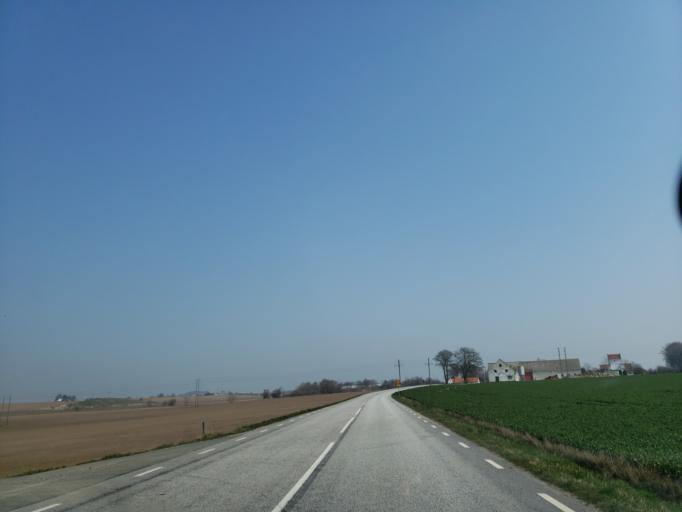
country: SE
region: Skane
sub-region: Simrishamns Kommun
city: Simrishamn
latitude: 55.4708
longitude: 14.2234
